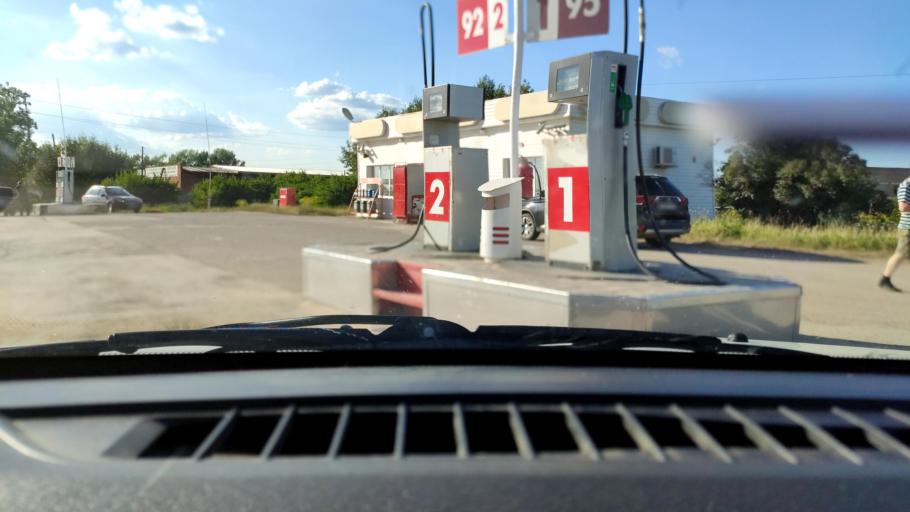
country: RU
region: Perm
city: Orda
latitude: 57.1873
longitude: 56.9174
